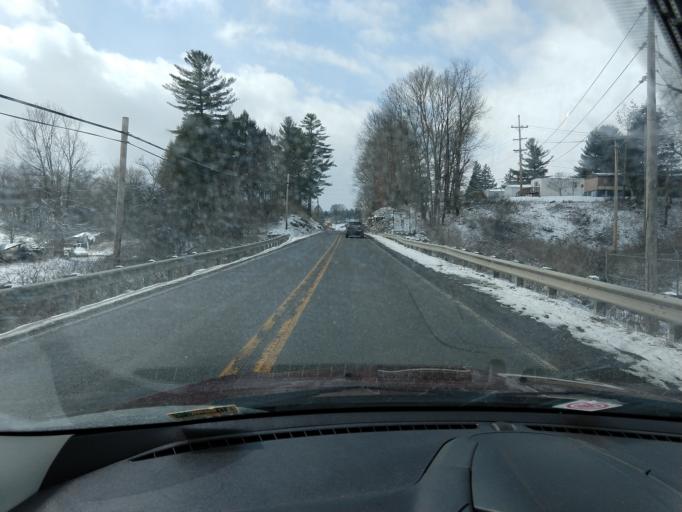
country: US
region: West Virginia
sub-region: Nicholas County
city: Craigsville
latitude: 38.3362
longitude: -80.6355
